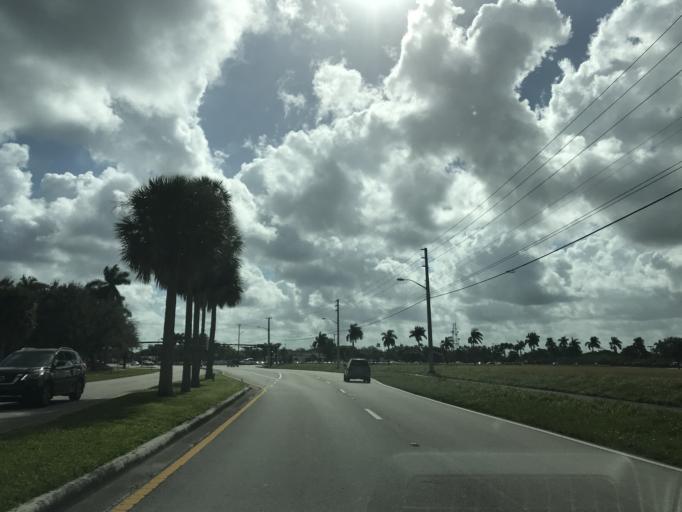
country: US
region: Florida
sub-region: Broward County
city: Margate
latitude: 26.2571
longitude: -80.1955
